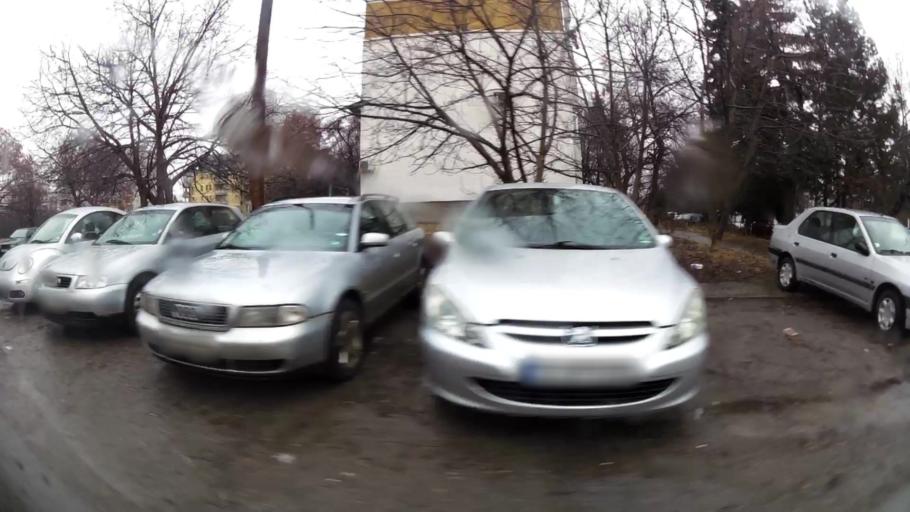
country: BG
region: Sofia-Capital
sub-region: Stolichna Obshtina
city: Sofia
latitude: 42.6545
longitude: 23.3698
